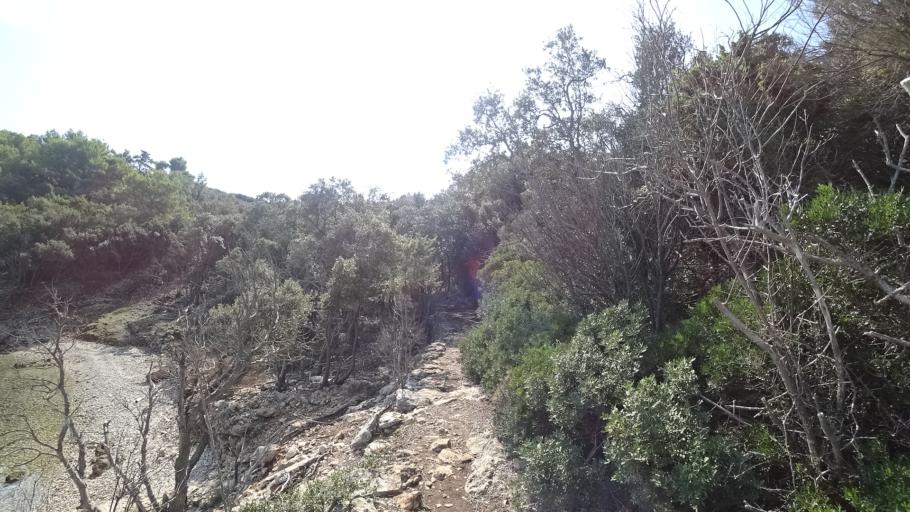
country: HR
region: Primorsko-Goranska
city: Mali Losinj
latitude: 44.5020
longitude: 14.5231
